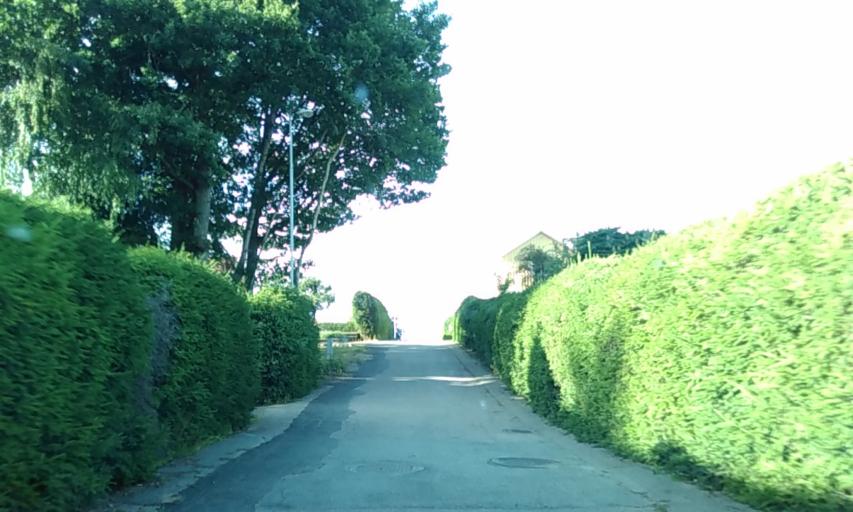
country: SE
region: Vaestra Goetaland
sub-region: Vara Kommun
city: Vara
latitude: 58.3239
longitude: 12.9207
